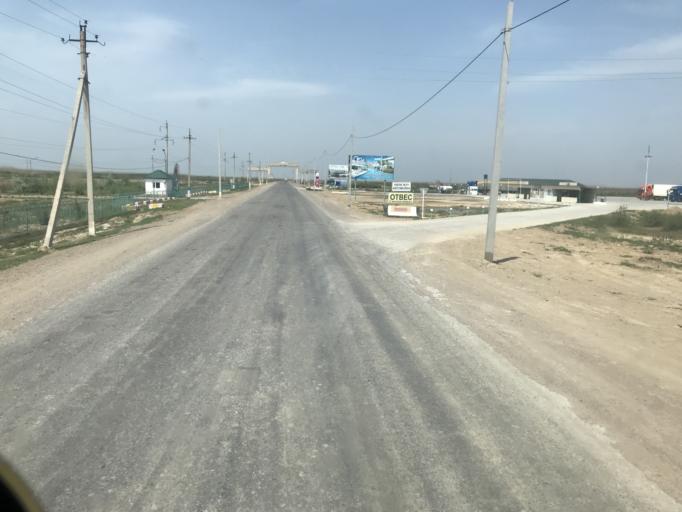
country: KZ
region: Ongtustik Qazaqstan
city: Asykata
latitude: 40.9614
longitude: 68.4609
